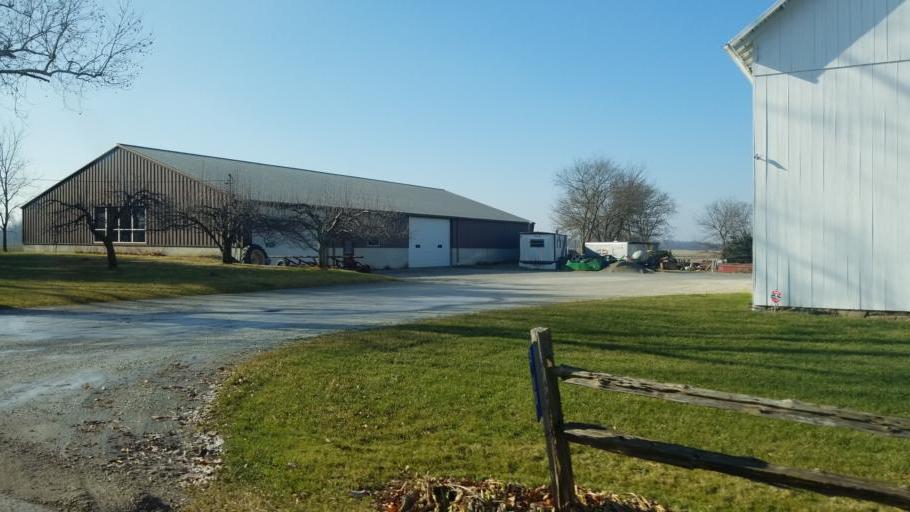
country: US
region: Ohio
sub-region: Seneca County
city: Tiffin
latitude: 41.0778
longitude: -83.1127
